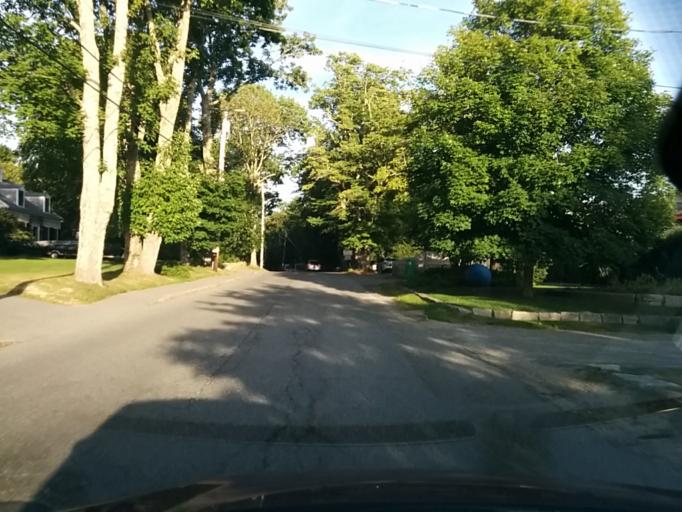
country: US
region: Maine
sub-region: Hancock County
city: Tremont
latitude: 44.2783
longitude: -68.3177
